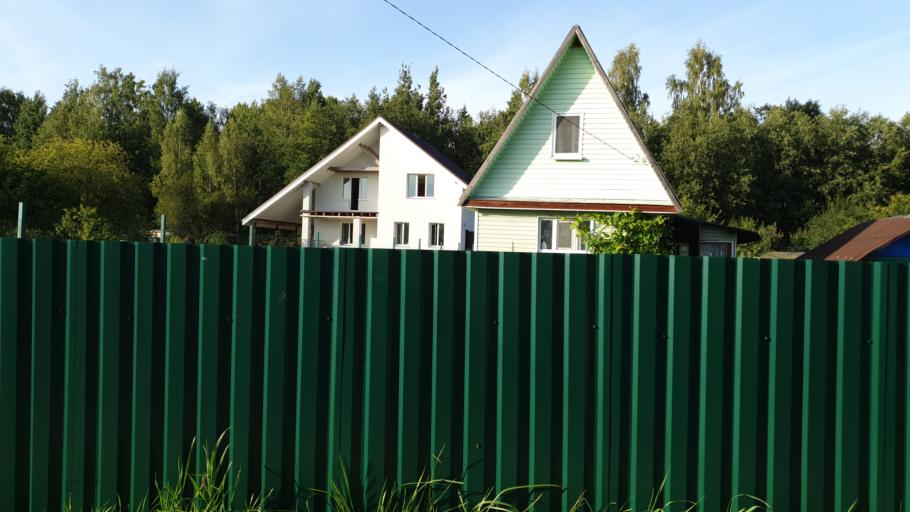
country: RU
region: Leningrad
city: Ivangorod
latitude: 59.4226
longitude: 28.3365
